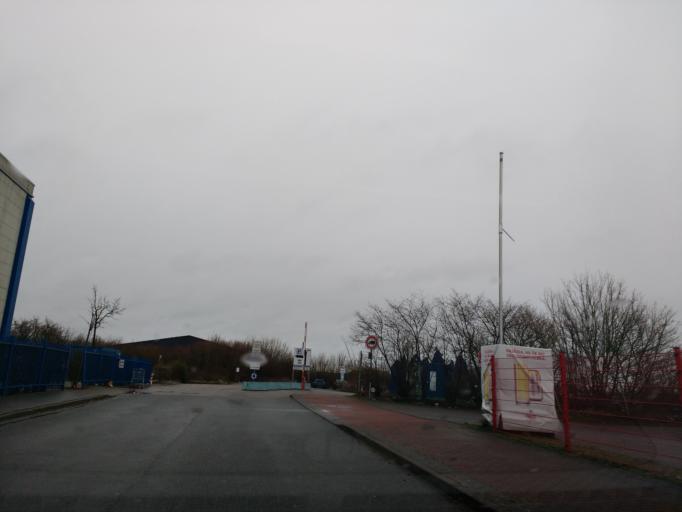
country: DE
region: Schleswig-Holstein
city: Fehmarn
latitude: 54.4458
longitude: 11.1813
